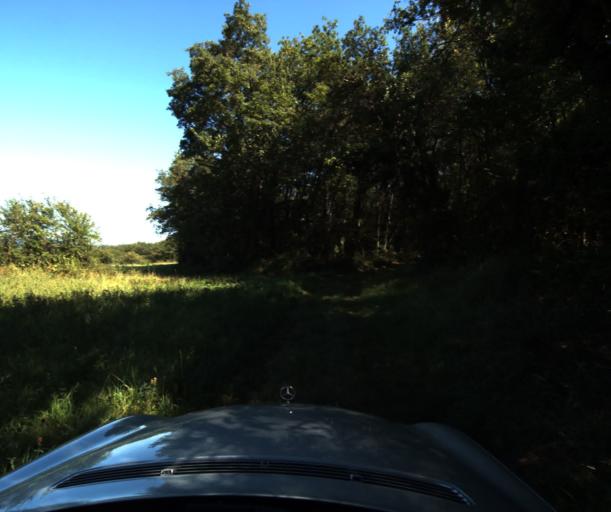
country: FR
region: Midi-Pyrenees
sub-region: Departement de l'Ariege
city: Belesta
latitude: 42.9658
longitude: 1.9233
